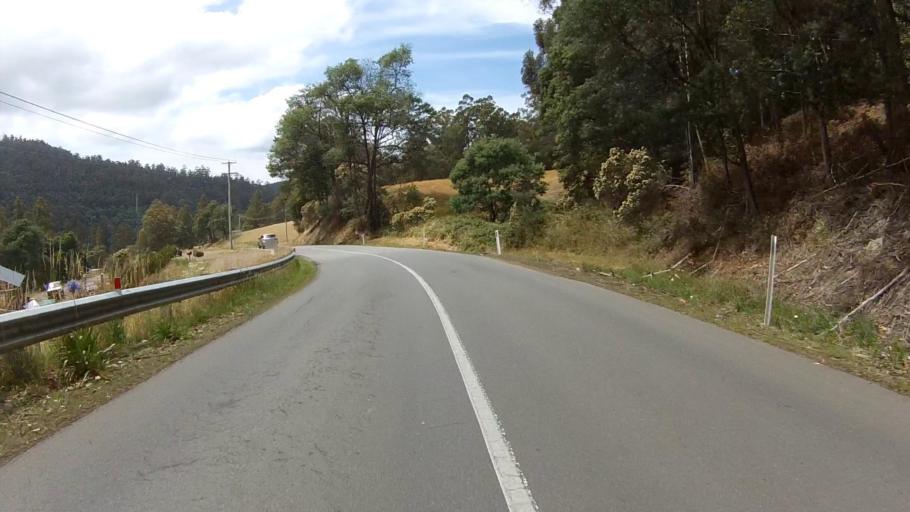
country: AU
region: Tasmania
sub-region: Kingborough
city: Kettering
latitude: -43.1059
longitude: 147.2047
